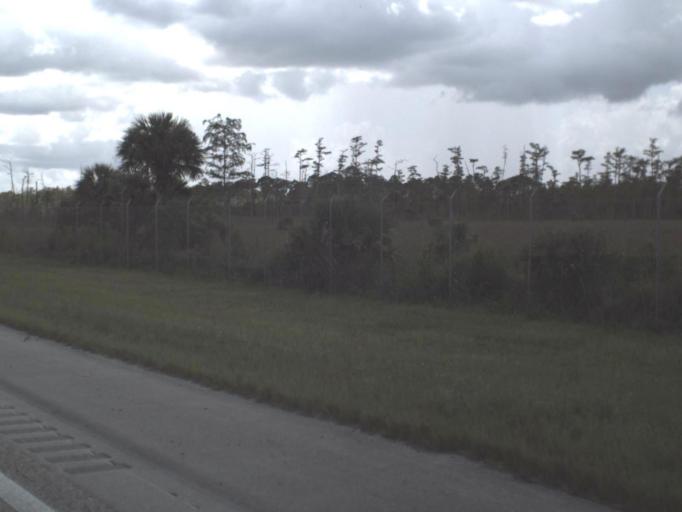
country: US
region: Florida
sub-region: Collier County
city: Immokalee
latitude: 26.1549
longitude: -81.3084
